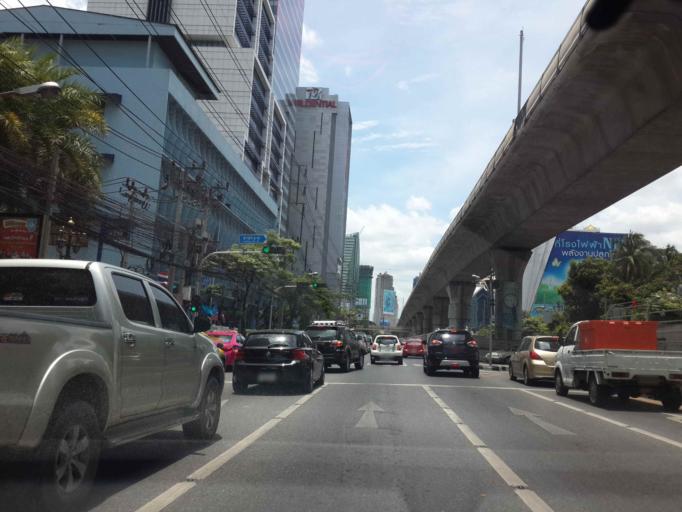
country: TH
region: Bangkok
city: Bang Rak
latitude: 13.7212
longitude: 100.5281
